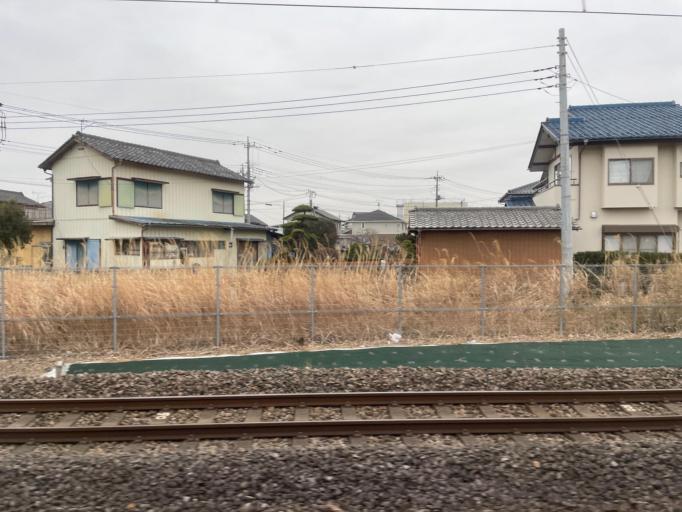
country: JP
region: Gunma
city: Maebashi-shi
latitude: 36.4136
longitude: 139.0327
